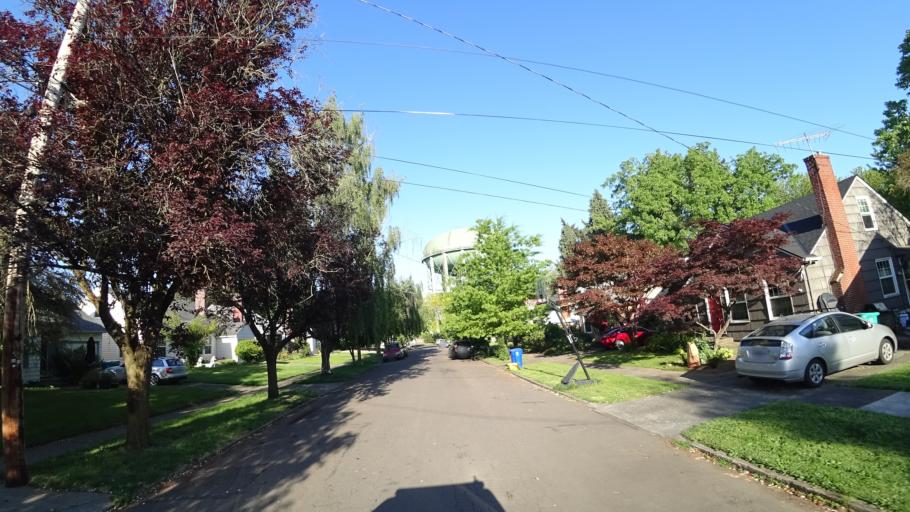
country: US
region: Oregon
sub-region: Multnomah County
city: Portland
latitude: 45.5569
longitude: -122.6891
